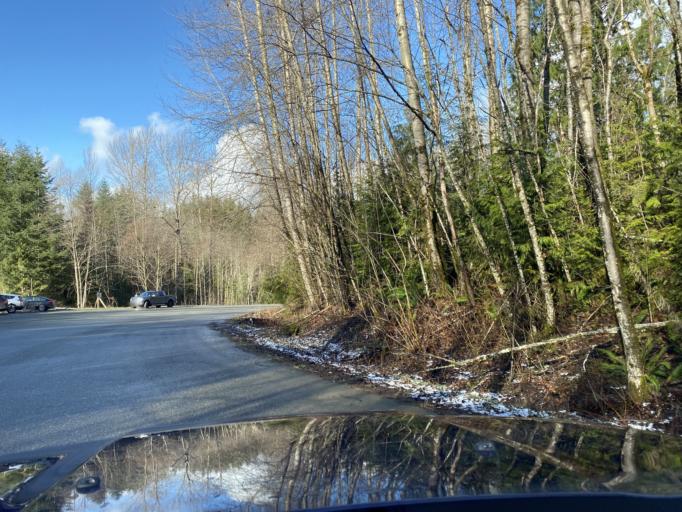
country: US
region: Washington
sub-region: King County
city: Snoqualmie
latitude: 47.5111
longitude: -121.8489
